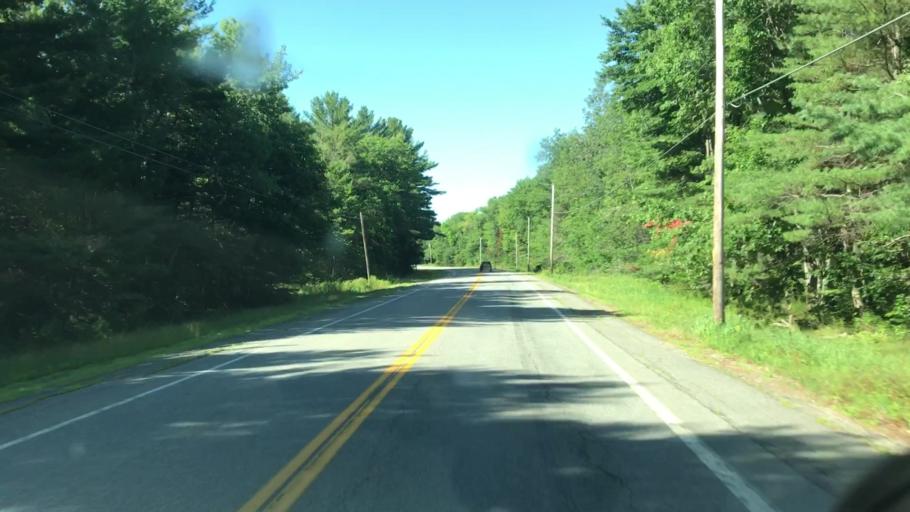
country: US
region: Maine
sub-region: Penobscot County
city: Howland
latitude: 45.2736
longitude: -68.6367
